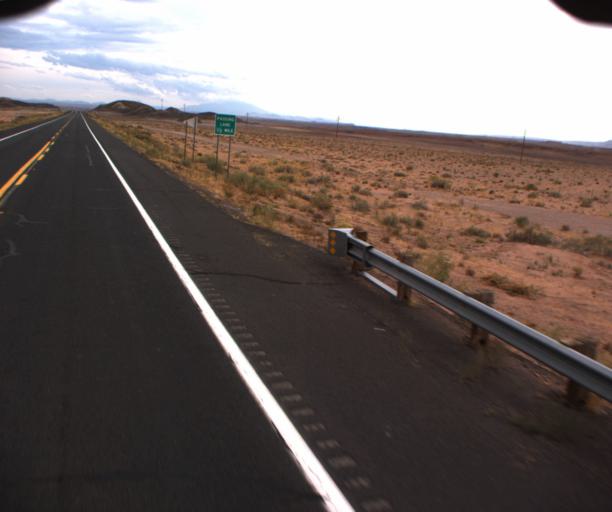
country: US
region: Arizona
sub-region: Coconino County
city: Tuba City
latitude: 35.9398
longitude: -111.4001
